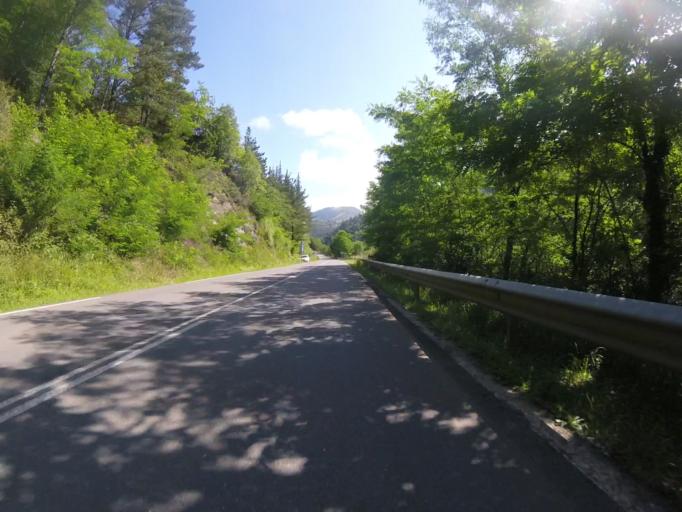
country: ES
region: Basque Country
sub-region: Provincia de Guipuzcoa
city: Beizama
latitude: 43.1165
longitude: -2.2291
